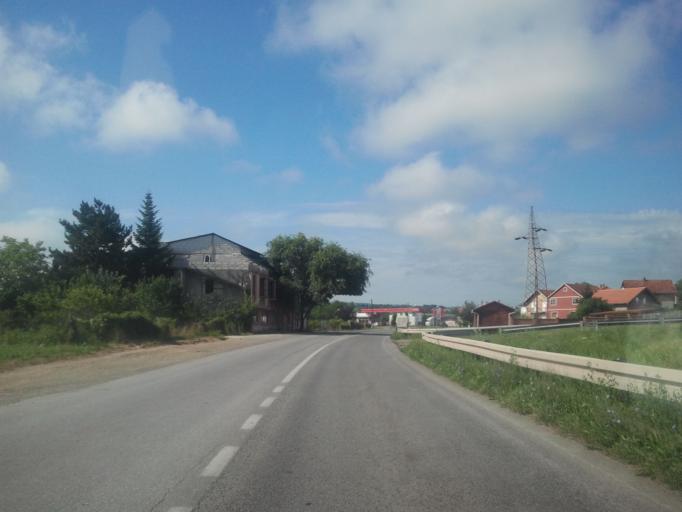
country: RS
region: Autonomna Pokrajina Vojvodina
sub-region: Juznobacki Okrug
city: Petrovaradin
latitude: 45.2320
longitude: 19.8845
